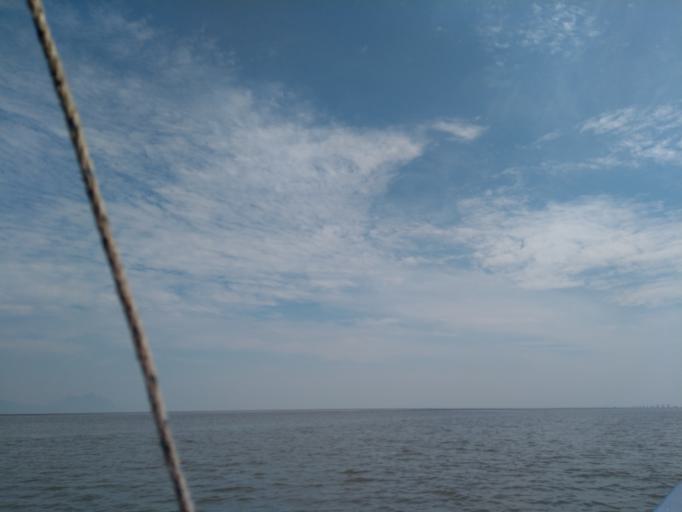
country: MY
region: Sarawak
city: Kuching
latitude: 1.6814
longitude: 110.4249
